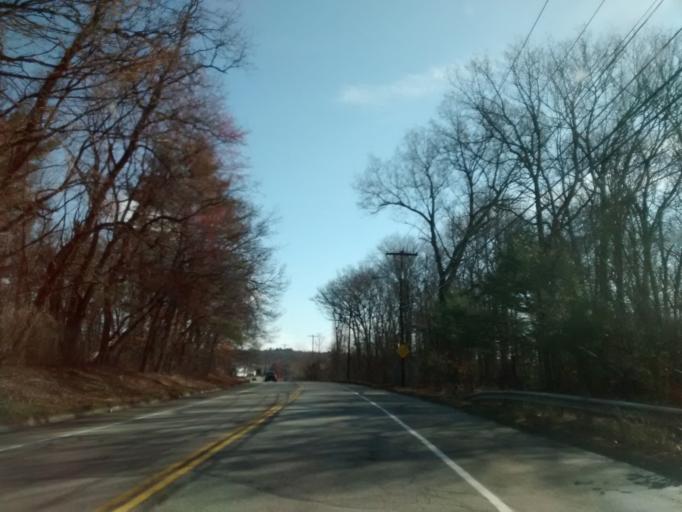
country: US
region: Massachusetts
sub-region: Worcester County
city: Whitinsville
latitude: 42.1111
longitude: -71.6853
